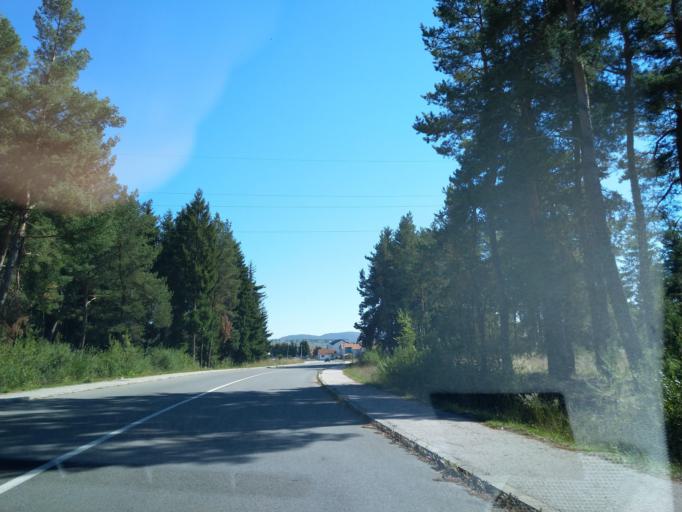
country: RS
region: Central Serbia
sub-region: Zlatiborski Okrug
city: Sjenica
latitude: 43.2721
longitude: 20.0177
